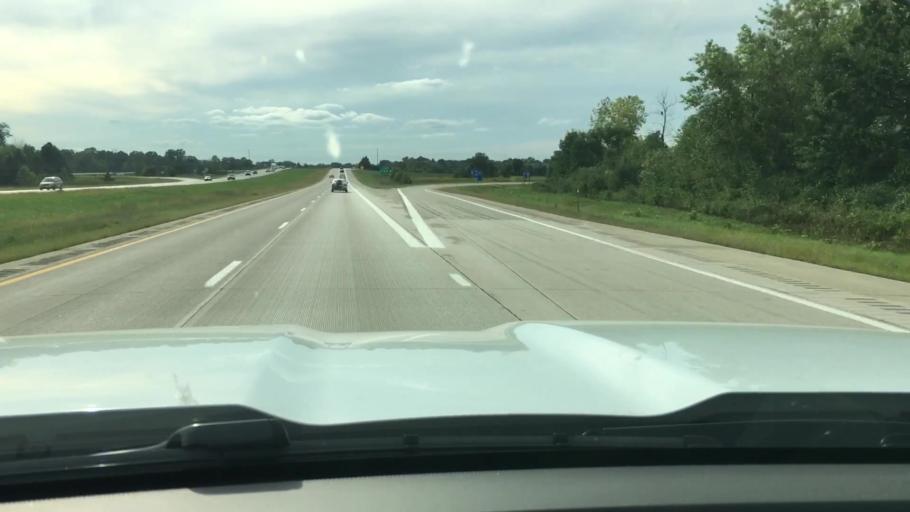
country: US
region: Michigan
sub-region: Genesee County
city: Davison
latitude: 43.0123
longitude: -83.5097
